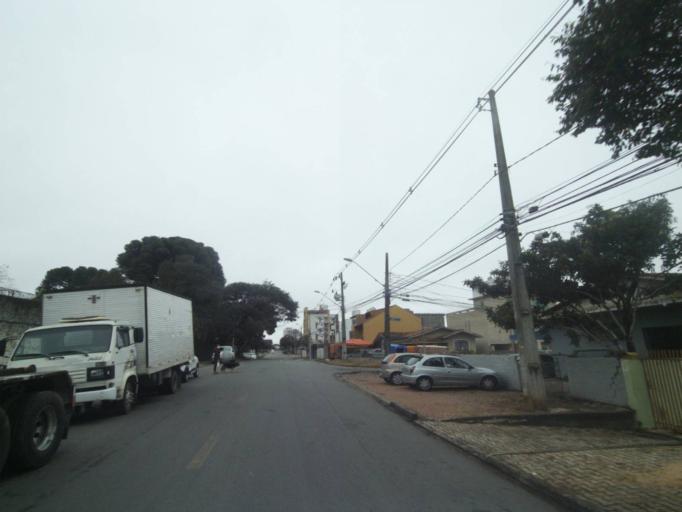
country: BR
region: Parana
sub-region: Curitiba
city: Curitiba
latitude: -25.5016
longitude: -49.3022
